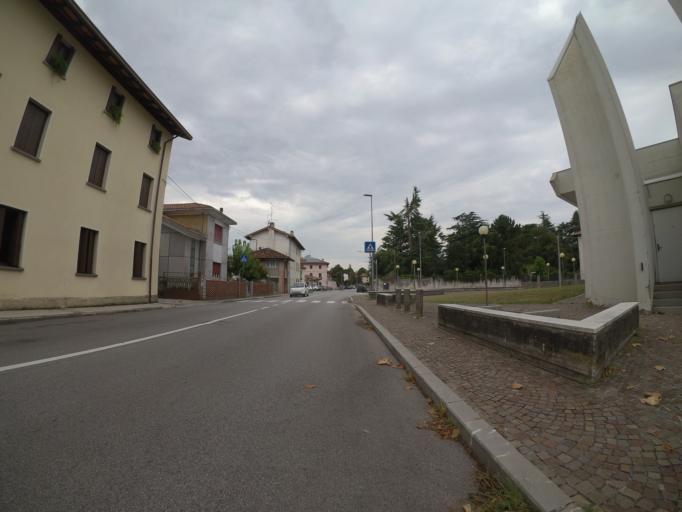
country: IT
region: Friuli Venezia Giulia
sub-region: Provincia di Udine
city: Codroipo
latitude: 45.9633
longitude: 12.9833
